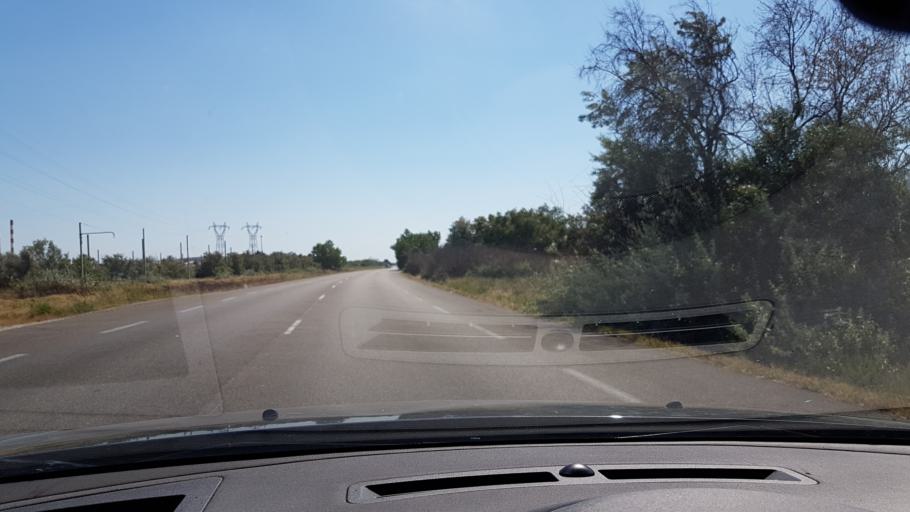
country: FR
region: Provence-Alpes-Cote d'Azur
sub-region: Departement des Bouches-du-Rhone
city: Port-Saint-Louis-du-Rhone
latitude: 43.4419
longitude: 4.8365
